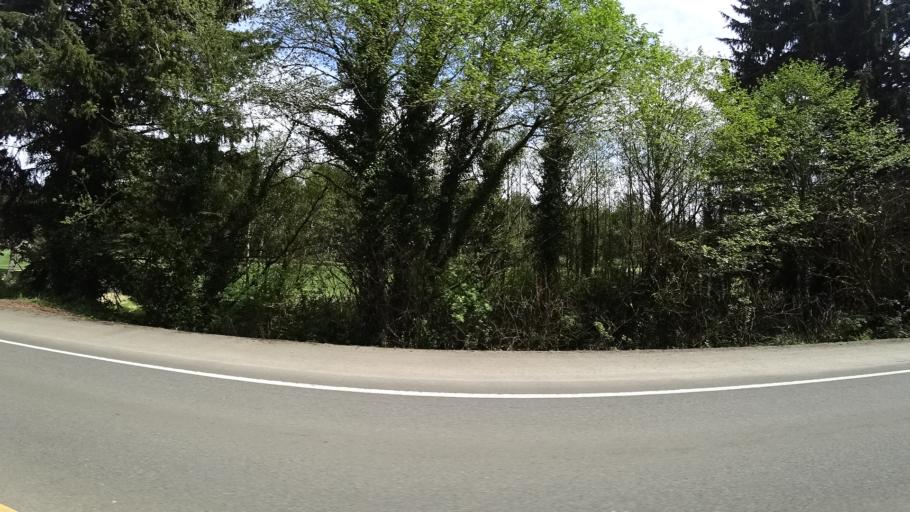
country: US
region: Oregon
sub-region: Lincoln County
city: Lincoln Beach
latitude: 44.8858
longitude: -124.0284
